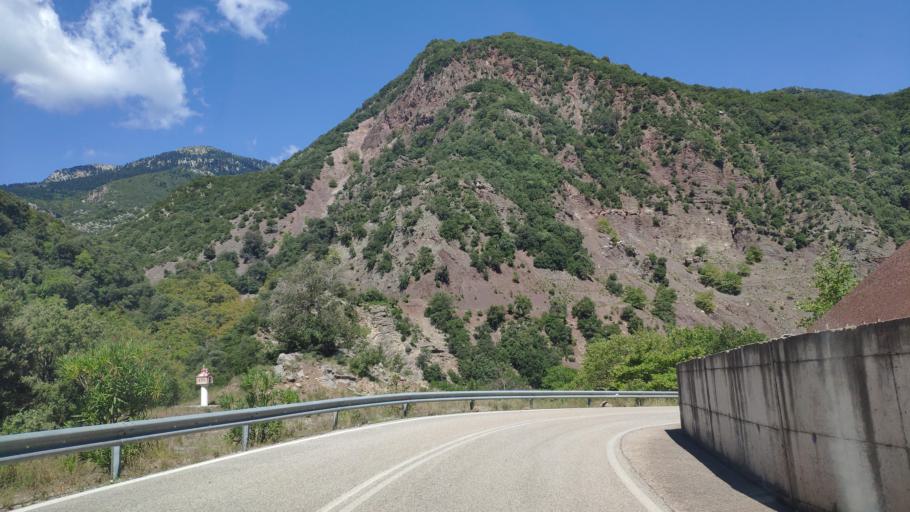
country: GR
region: Central Greece
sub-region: Nomos Evrytanias
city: Kerasochori
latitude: 39.0468
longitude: 21.5965
